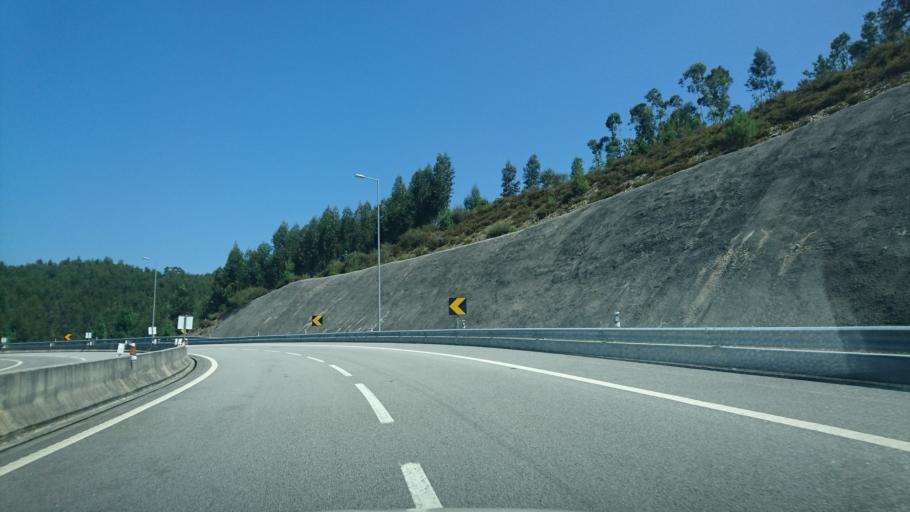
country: PT
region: Porto
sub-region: Gondomar
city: Foz do Sousa
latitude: 41.0943
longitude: -8.4542
